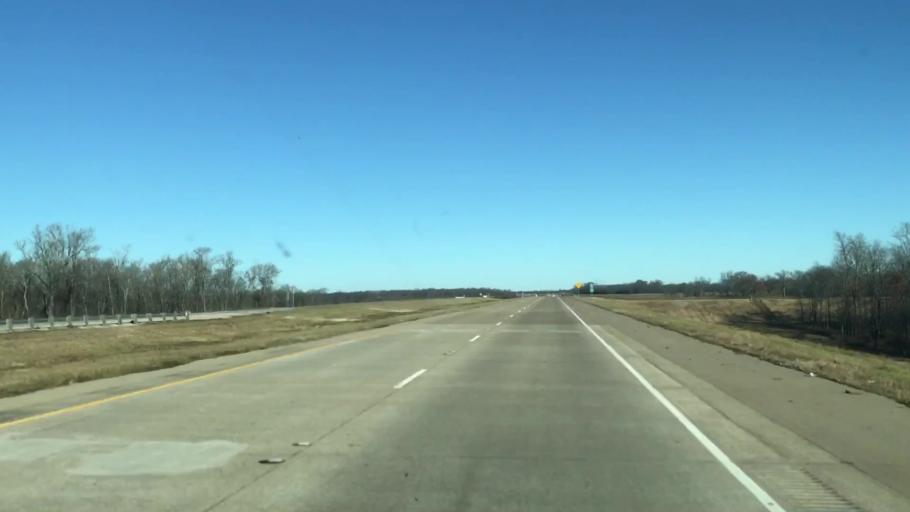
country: US
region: Louisiana
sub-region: Caddo Parish
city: Blanchard
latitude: 32.6273
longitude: -93.8367
